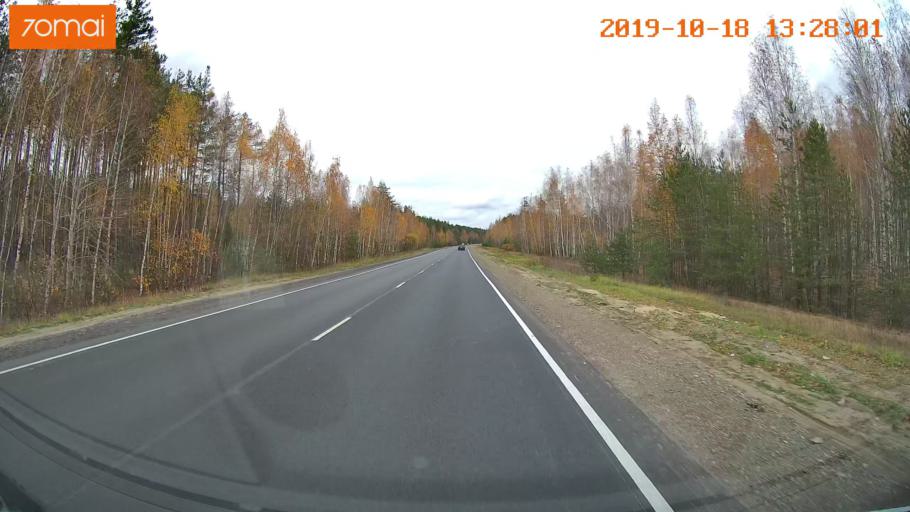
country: RU
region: Rjazan
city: Solotcha
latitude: 54.7728
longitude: 39.8605
